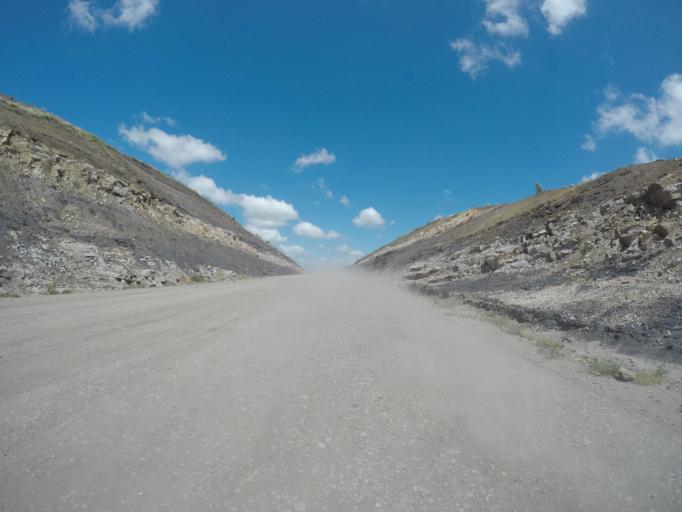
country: ZA
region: KwaZulu-Natal
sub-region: uThungulu District Municipality
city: Empangeni
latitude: -28.6273
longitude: 31.7587
